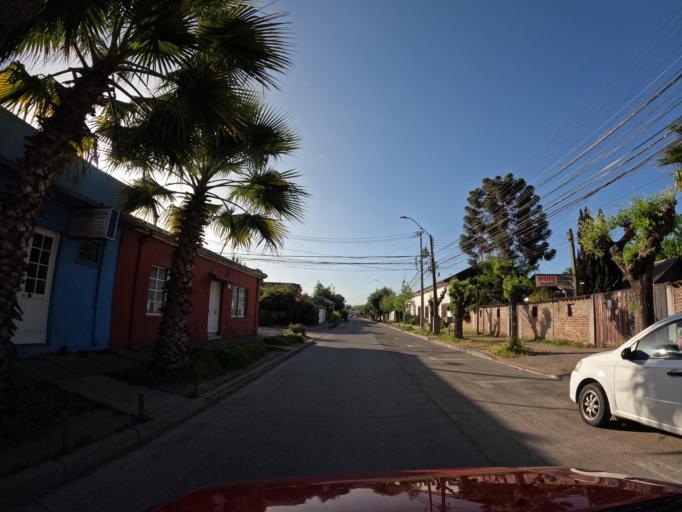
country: CL
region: O'Higgins
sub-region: Provincia de Colchagua
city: Santa Cruz
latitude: -34.6386
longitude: -71.3668
